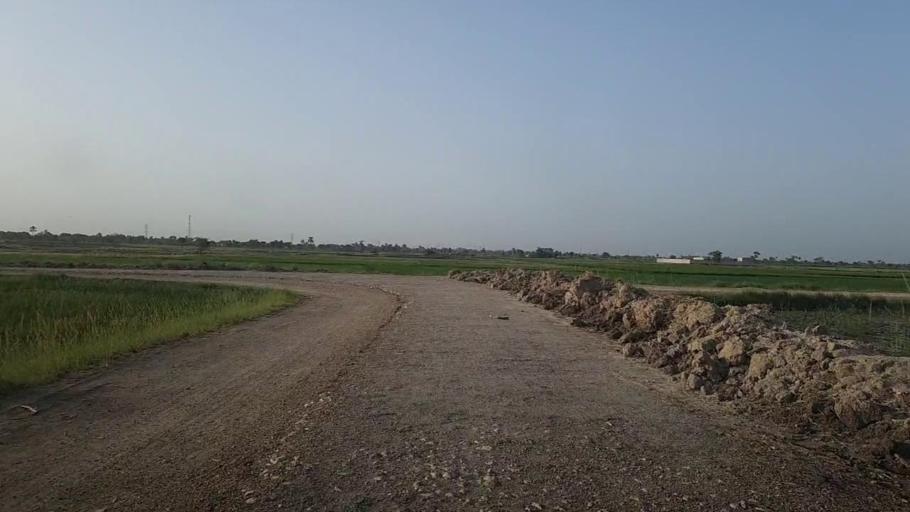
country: PK
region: Sindh
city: Naushahro Firoz
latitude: 26.8083
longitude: 68.1116
